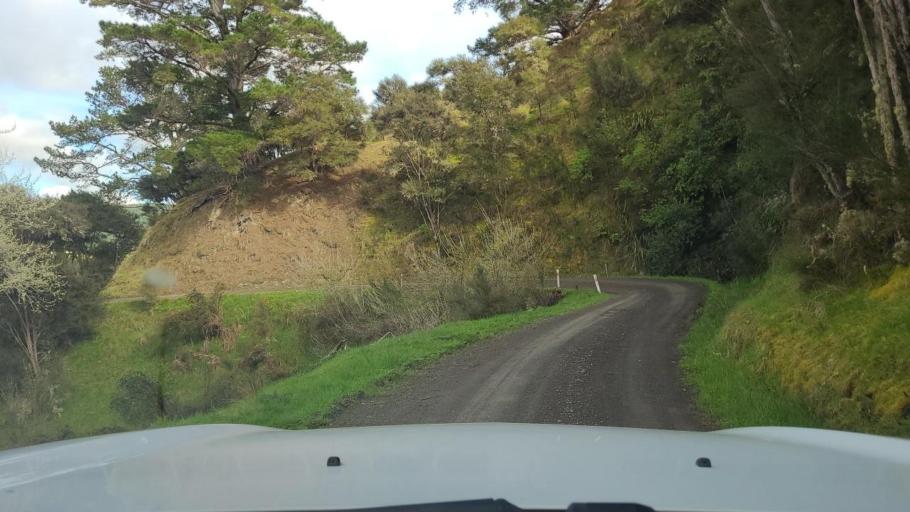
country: NZ
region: Wellington
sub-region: South Wairarapa District
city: Waipawa
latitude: -41.2610
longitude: 175.6889
